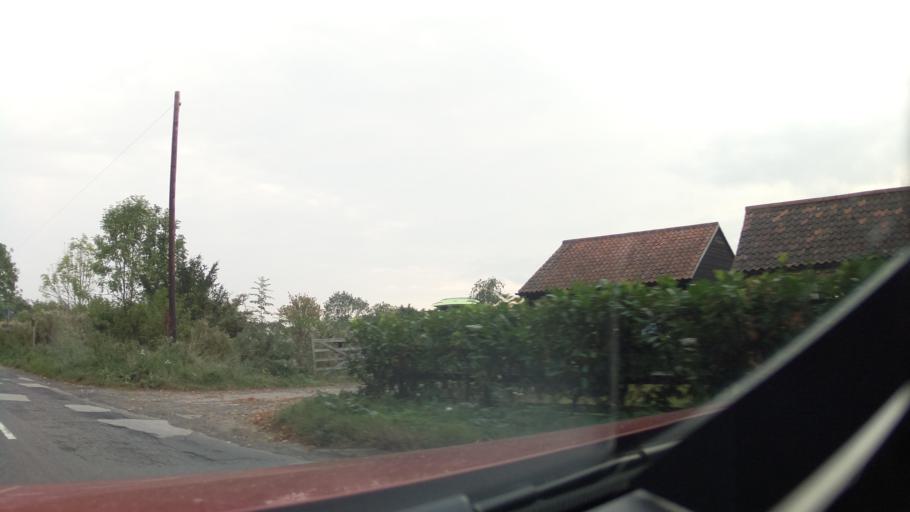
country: GB
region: England
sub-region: Lincolnshire
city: Skellingthorpe
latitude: 53.1421
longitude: -0.6458
